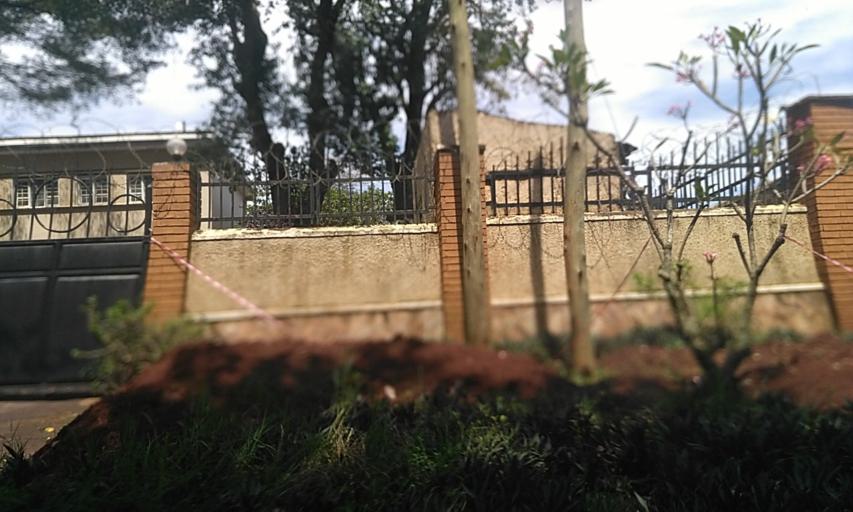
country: UG
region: Central Region
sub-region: Kampala District
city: Kampala
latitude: 0.3348
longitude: 32.6009
